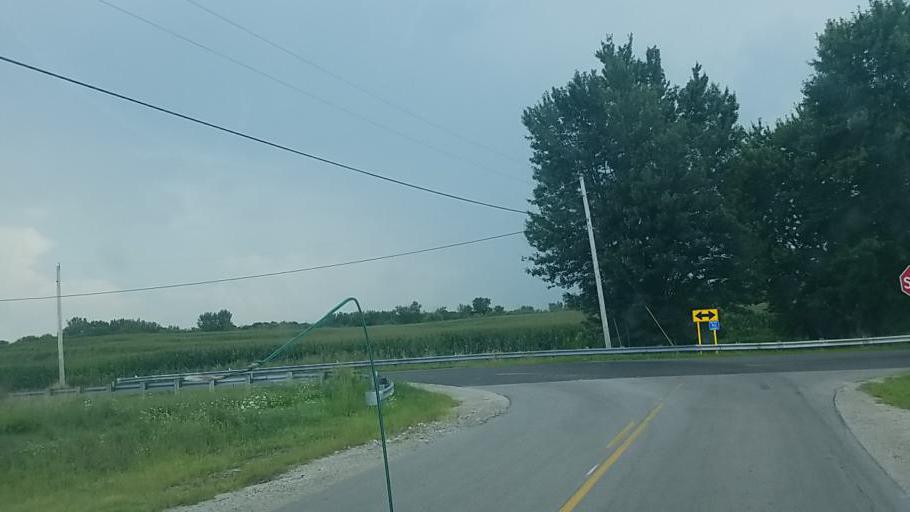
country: US
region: Ohio
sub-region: Medina County
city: Lodi
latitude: 41.0008
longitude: -82.0190
